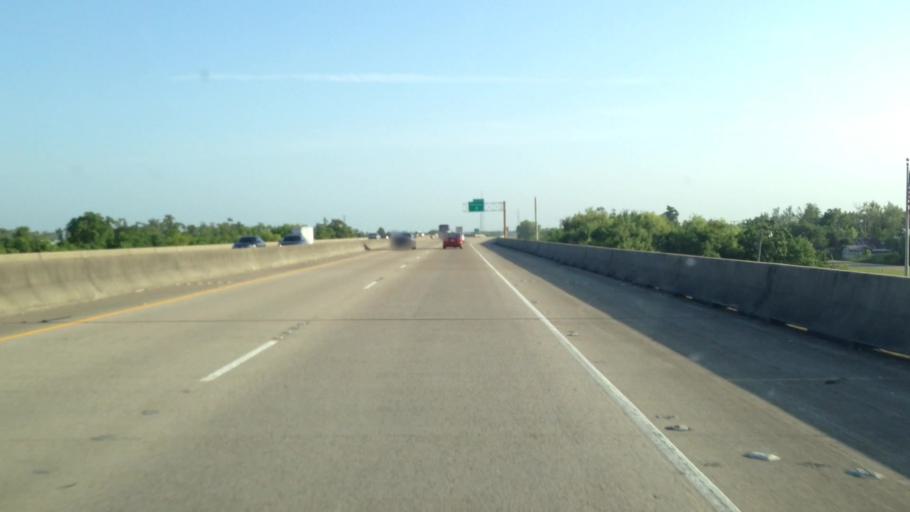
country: US
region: Louisiana
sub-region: Tangipahoa Parish
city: Ponchatoula
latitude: 30.2906
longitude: -90.4029
